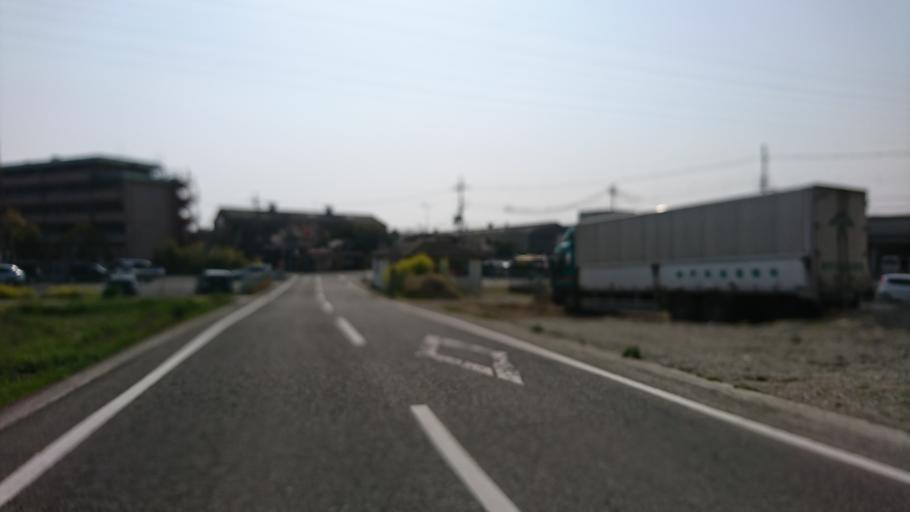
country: JP
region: Hyogo
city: Kakogawacho-honmachi
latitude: 34.7327
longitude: 134.8908
